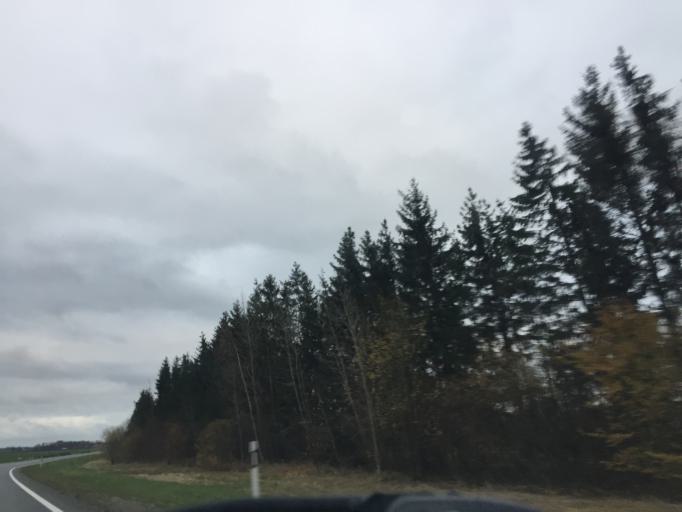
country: LV
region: Jaunpils
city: Jaunpils
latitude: 56.6641
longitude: 22.9117
